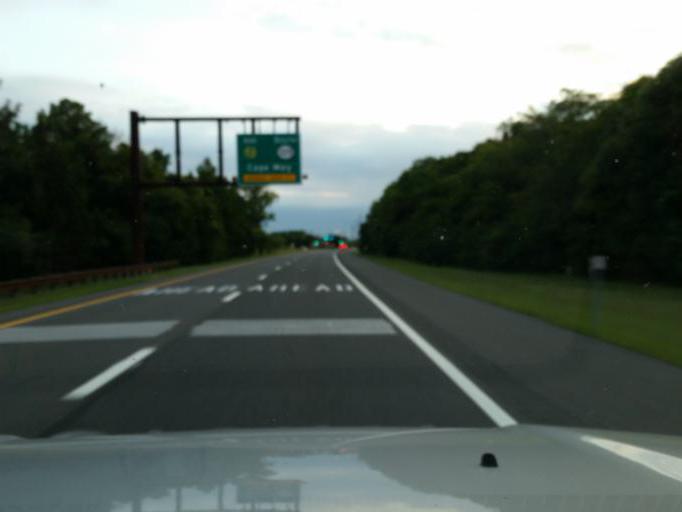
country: US
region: New Jersey
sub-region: Cape May County
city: Erma
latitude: 38.9642
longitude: -74.9015
